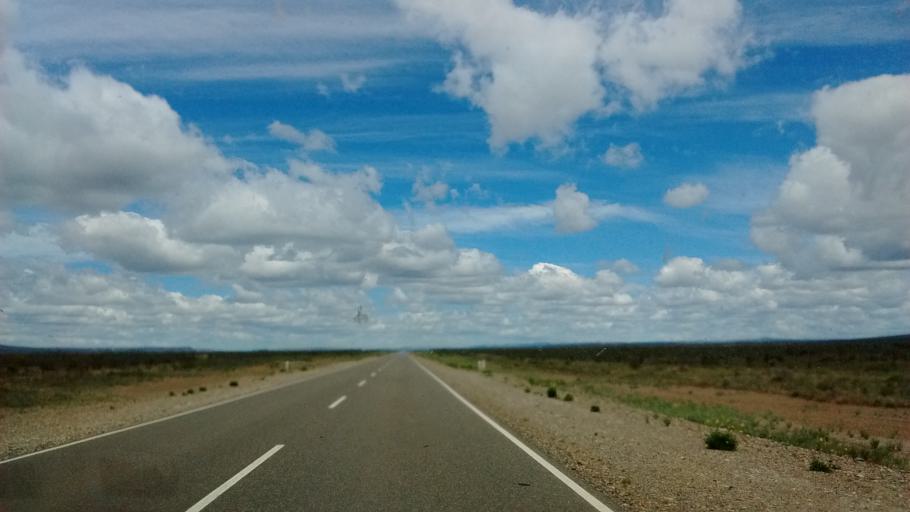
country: AR
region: Neuquen
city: Piedra del Aguila
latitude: -39.8112
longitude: -69.7160
